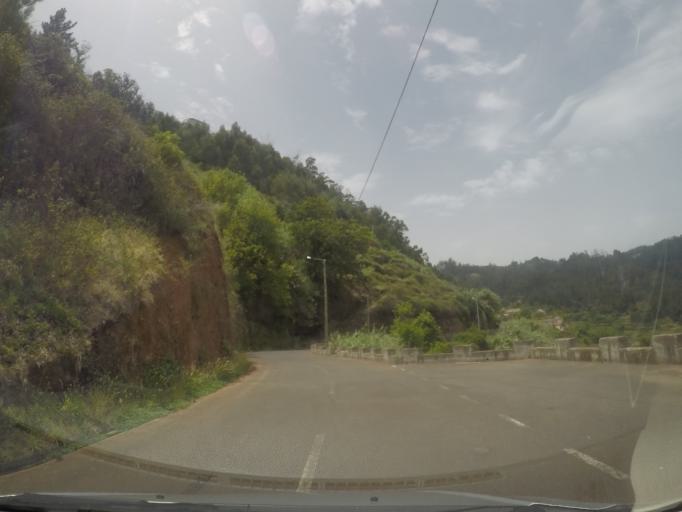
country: PT
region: Madeira
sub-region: Santa Cruz
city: Camacha
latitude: 32.6771
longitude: -16.8375
